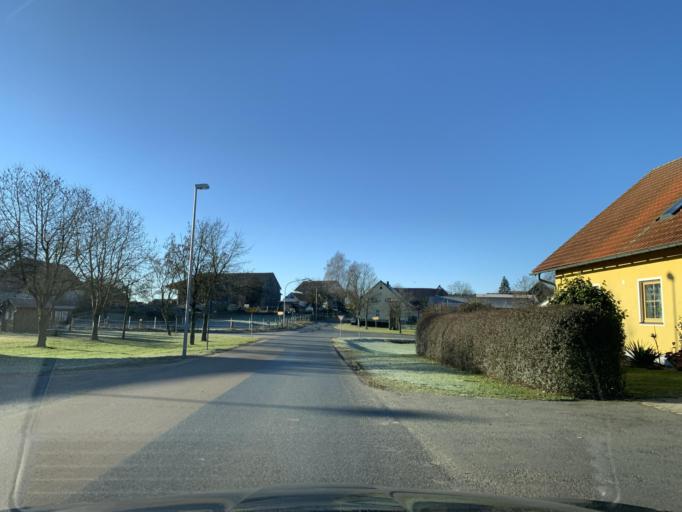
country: DE
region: Bavaria
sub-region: Upper Palatinate
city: Oberviechtach
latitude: 49.4552
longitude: 12.4477
